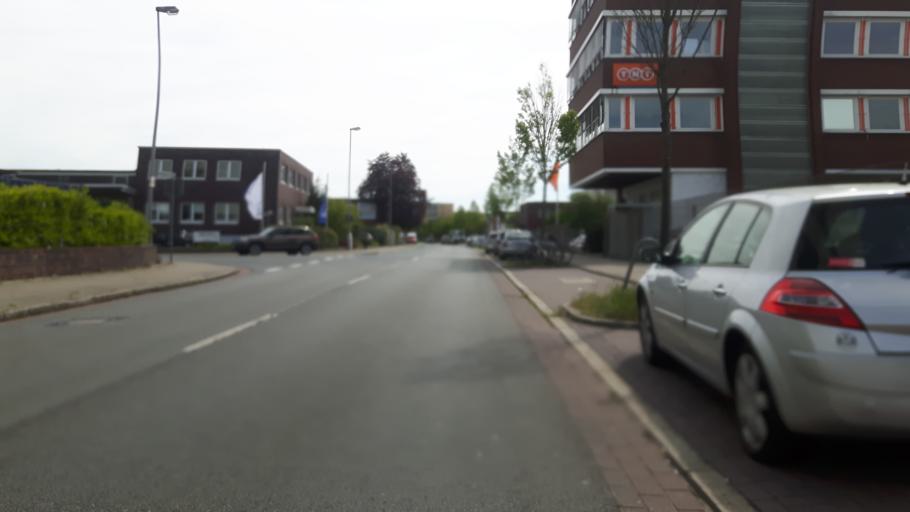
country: DE
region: Lower Saxony
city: Stuhr
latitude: 53.0599
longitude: 8.7732
